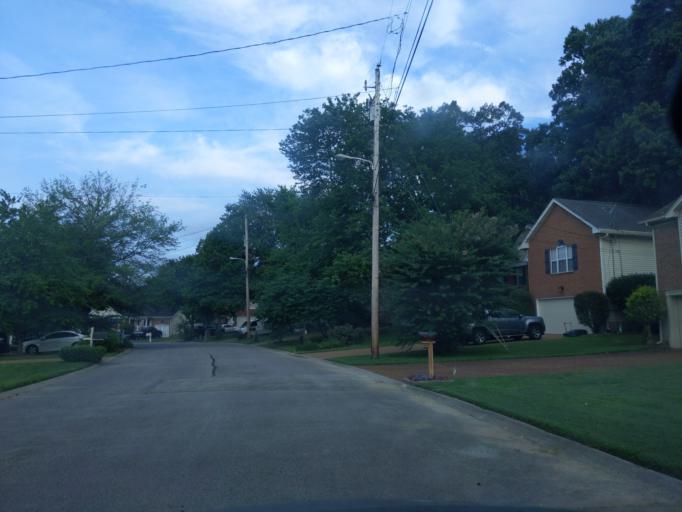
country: US
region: Tennessee
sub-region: Wilson County
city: Green Hill
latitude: 36.1856
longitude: -86.5974
